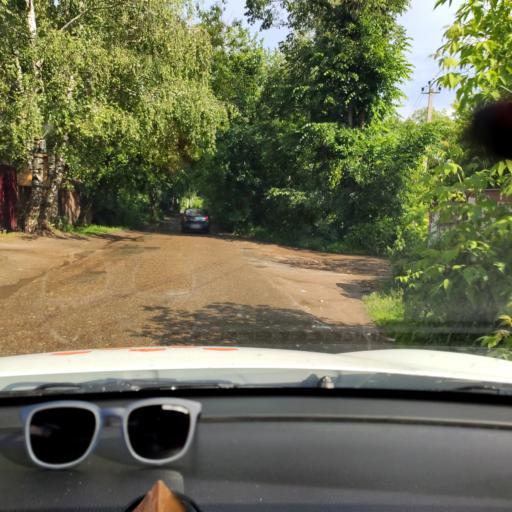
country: RU
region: Tatarstan
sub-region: Zelenodol'skiy Rayon
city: Vasil'yevo
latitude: 55.8273
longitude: 48.7610
